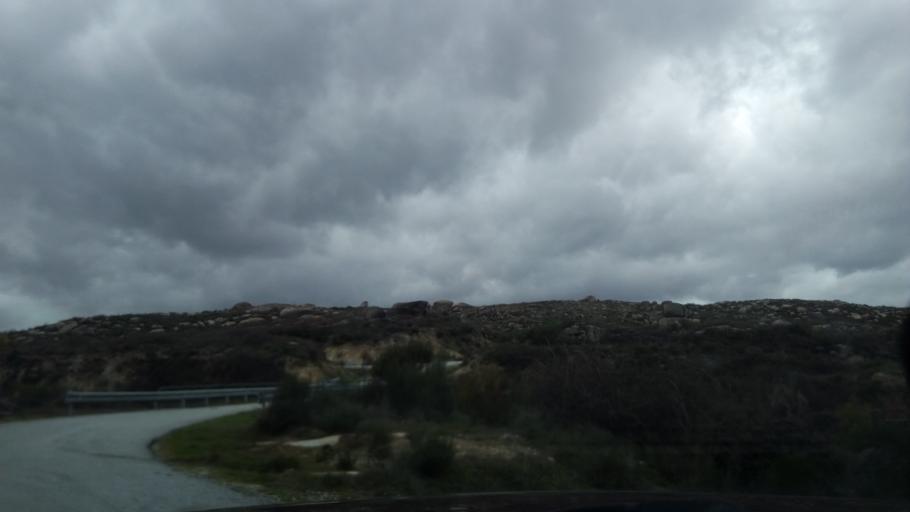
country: PT
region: Guarda
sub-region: Fornos de Algodres
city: Fornos de Algodres
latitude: 40.5879
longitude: -7.5672
